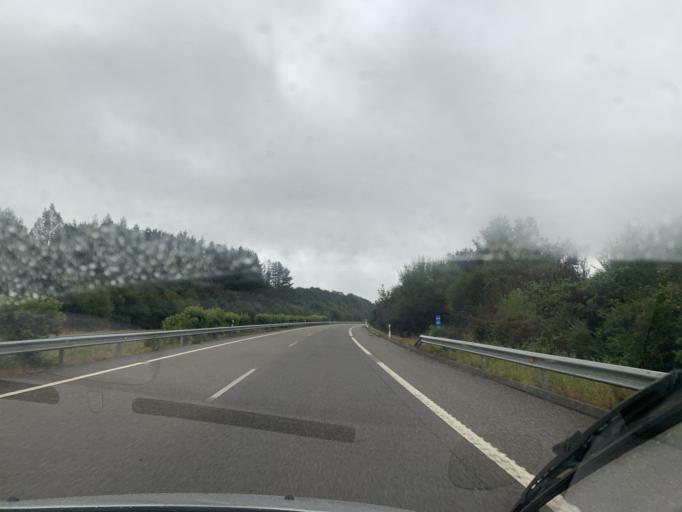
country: ES
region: Galicia
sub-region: Provincia de Lugo
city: Abadin
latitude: 43.3480
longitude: -7.5048
